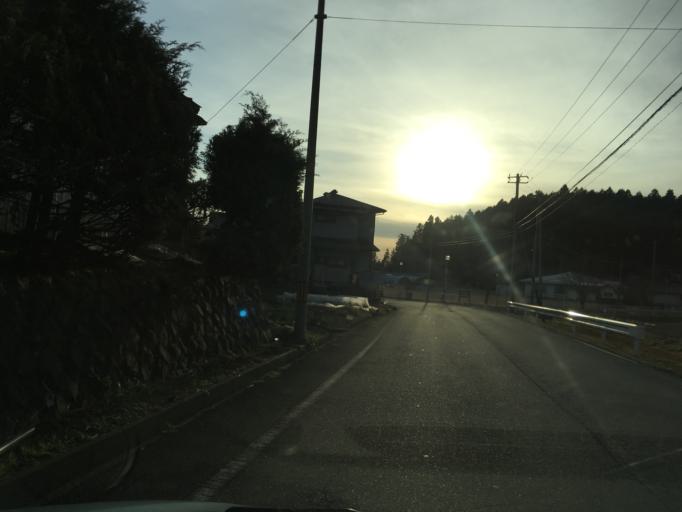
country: JP
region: Iwate
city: Ichinoseki
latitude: 38.7540
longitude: 141.1652
